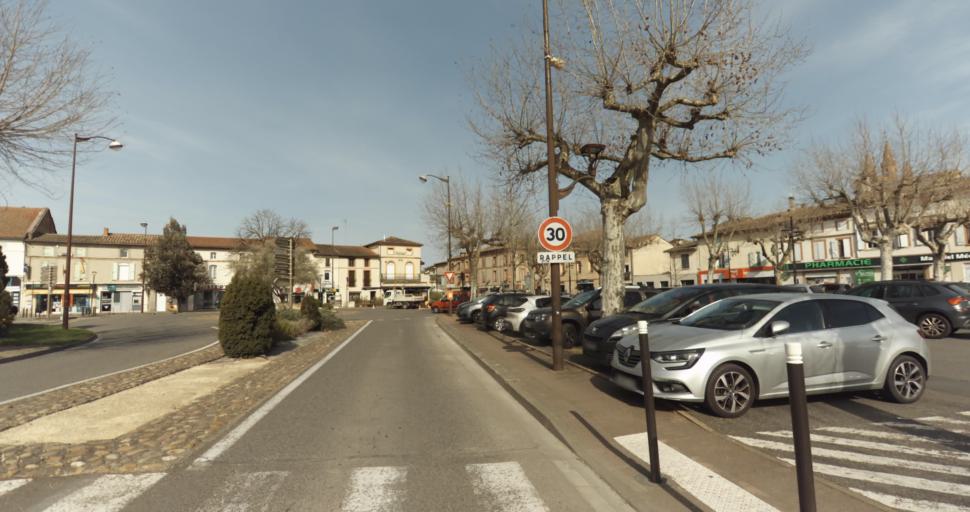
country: FR
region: Midi-Pyrenees
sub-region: Departement du Tarn
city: Saint-Sulpice-la-Pointe
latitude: 43.7737
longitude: 1.6864
